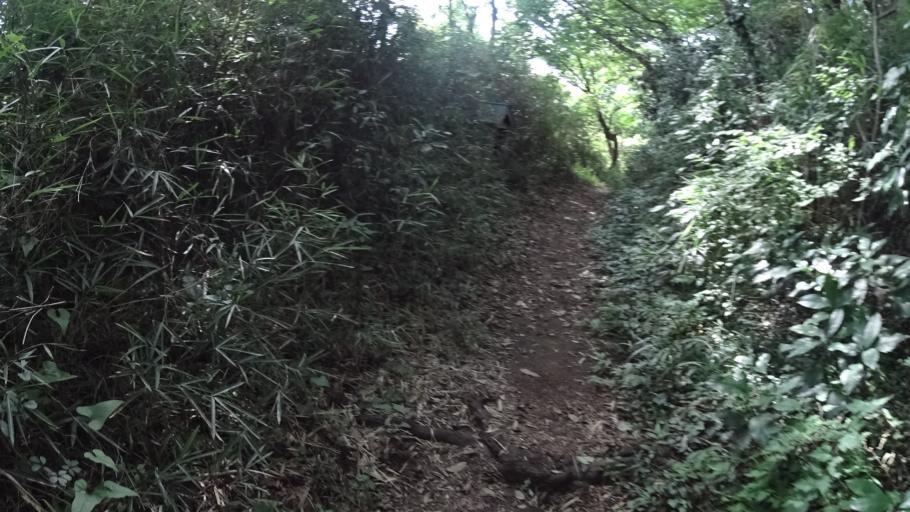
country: JP
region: Kanagawa
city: Zushi
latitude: 35.3124
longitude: 139.6101
